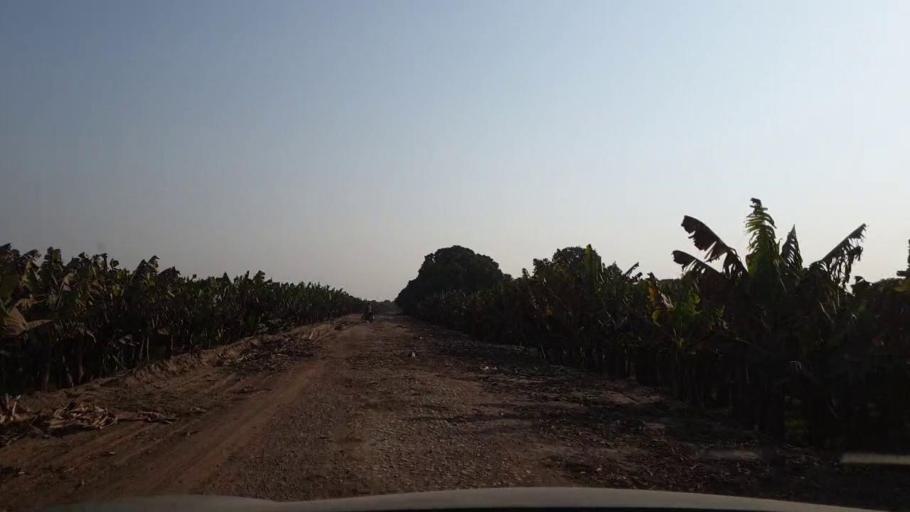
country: PK
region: Sindh
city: Tando Allahyar
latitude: 25.5727
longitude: 68.7642
